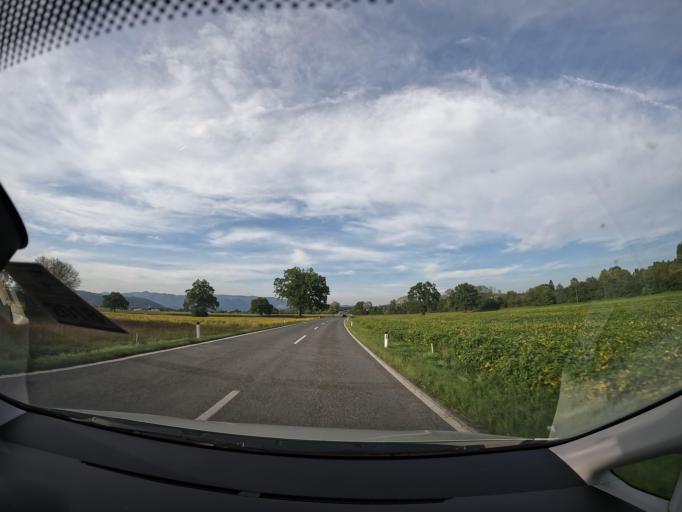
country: AT
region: Carinthia
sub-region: Politischer Bezirk Volkermarkt
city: Eberndorf
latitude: 46.6063
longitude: 14.6330
